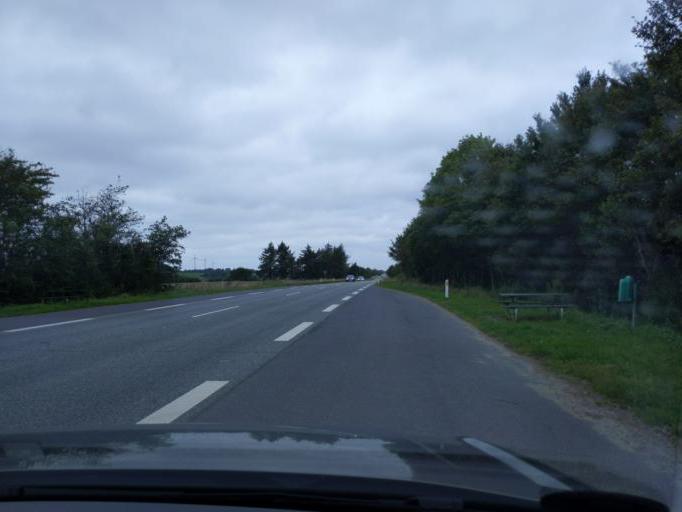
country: DK
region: Central Jutland
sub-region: Randers Kommune
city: Spentrup
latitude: 56.5259
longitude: 9.9269
